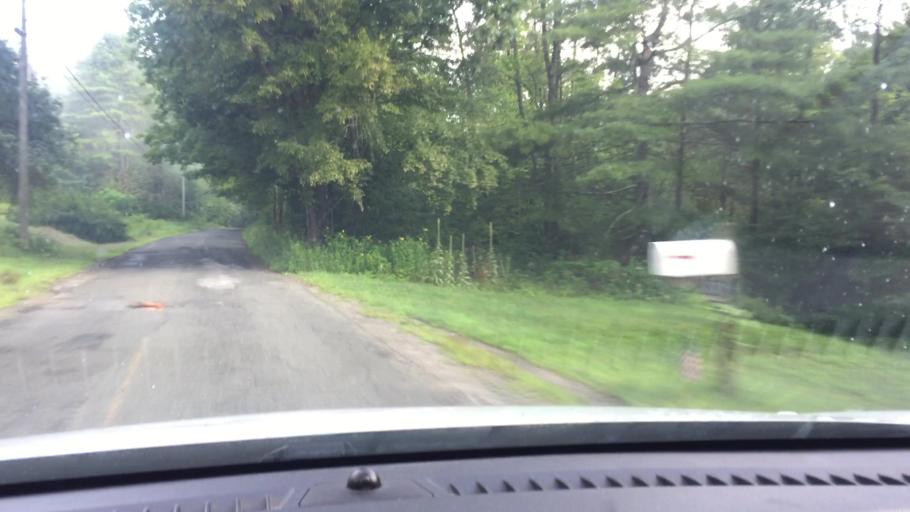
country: US
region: Massachusetts
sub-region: Hampshire County
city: Chesterfield
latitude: 42.3152
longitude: -72.9235
